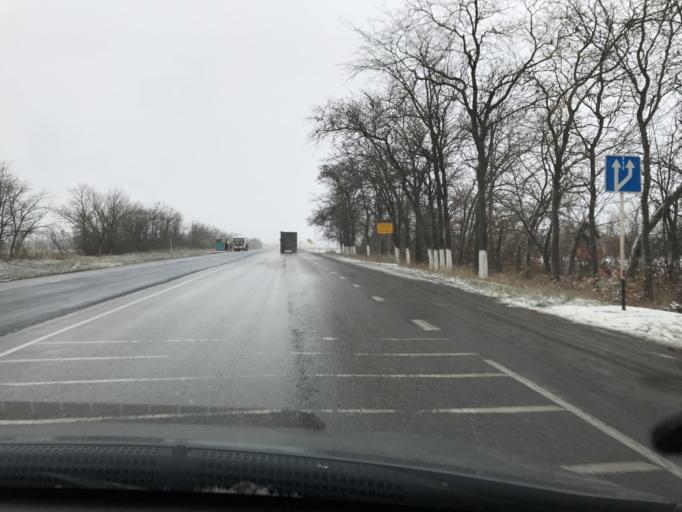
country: RU
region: Rostov
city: Mechetinskaya
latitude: 46.7962
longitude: 40.3767
